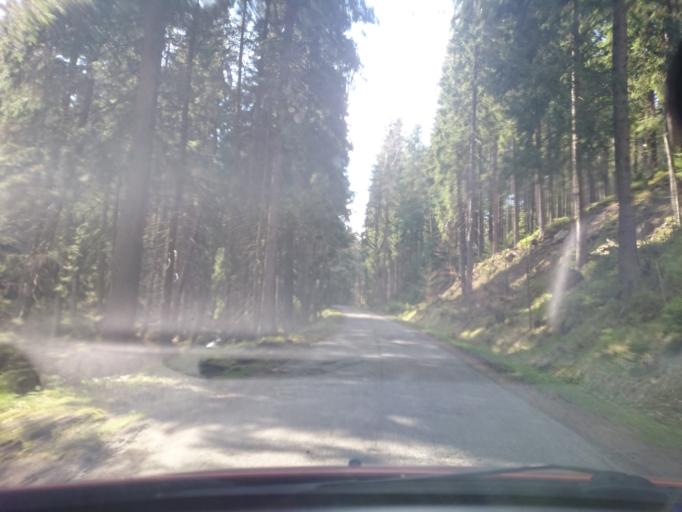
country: PL
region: Lower Silesian Voivodeship
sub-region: Powiat klodzki
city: Polanica-Zdroj
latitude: 50.3078
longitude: 16.5124
